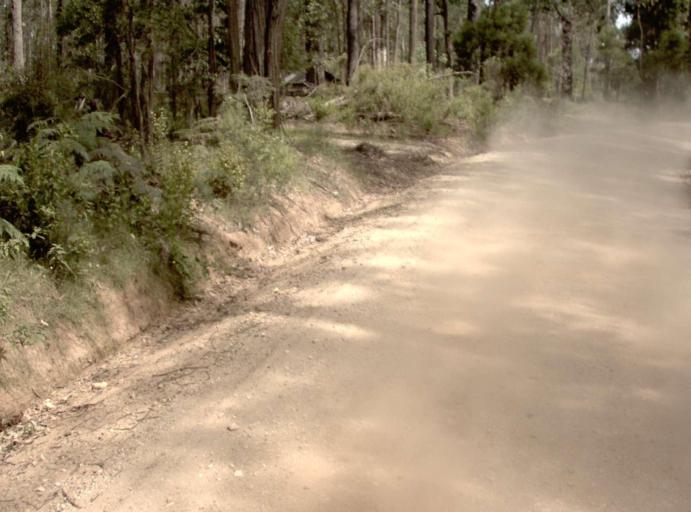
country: AU
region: Victoria
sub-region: East Gippsland
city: Lakes Entrance
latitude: -37.6309
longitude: 148.6762
